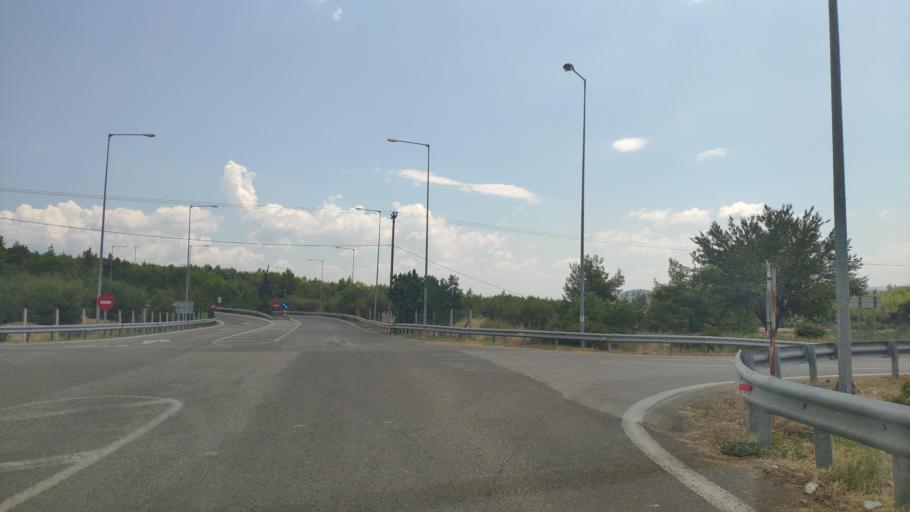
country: GR
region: Central Greece
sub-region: Nomos Fthiotidos
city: Martinon
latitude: 38.5948
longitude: 23.1895
